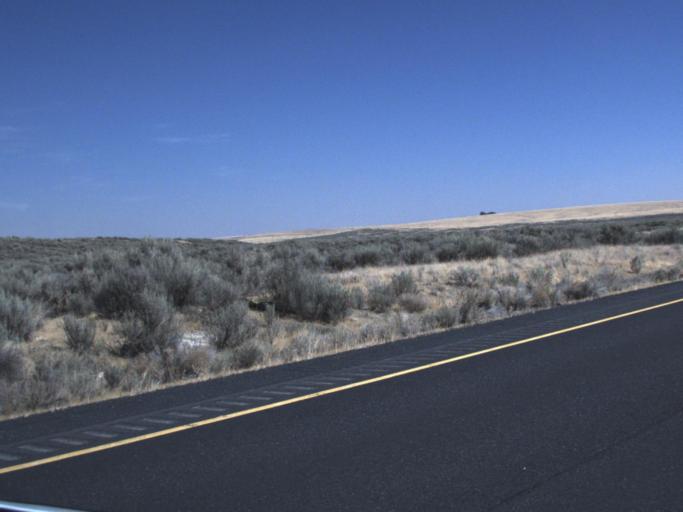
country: US
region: Washington
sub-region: Grant County
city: Warden
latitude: 47.0870
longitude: -118.8899
